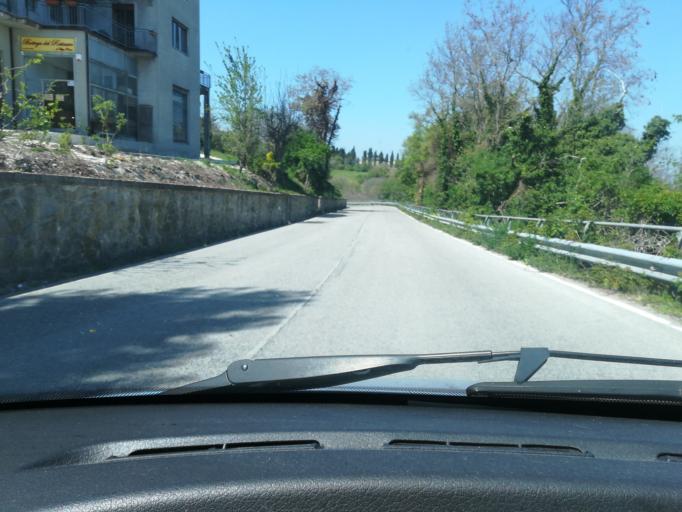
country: IT
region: The Marches
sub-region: Provincia di Macerata
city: Cingoli
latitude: 43.3792
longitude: 13.2155
